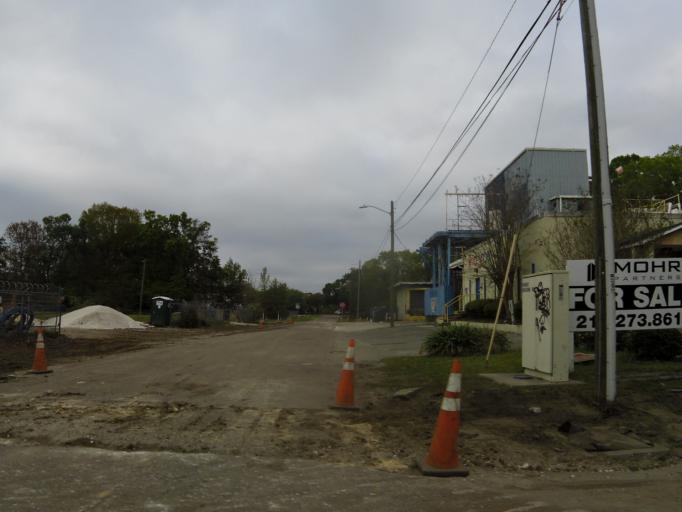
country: US
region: Florida
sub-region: Duval County
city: Jacksonville
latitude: 30.3224
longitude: -81.7262
